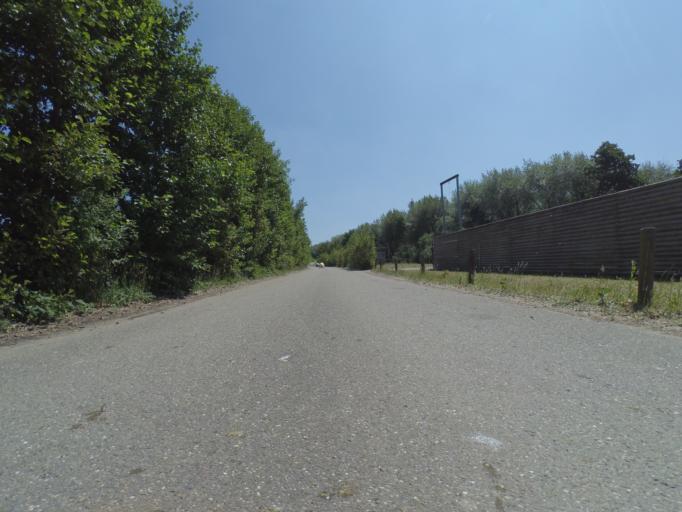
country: NL
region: Zeeland
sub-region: Gemeente Tholen
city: Tholen
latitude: 51.5000
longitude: 4.1883
